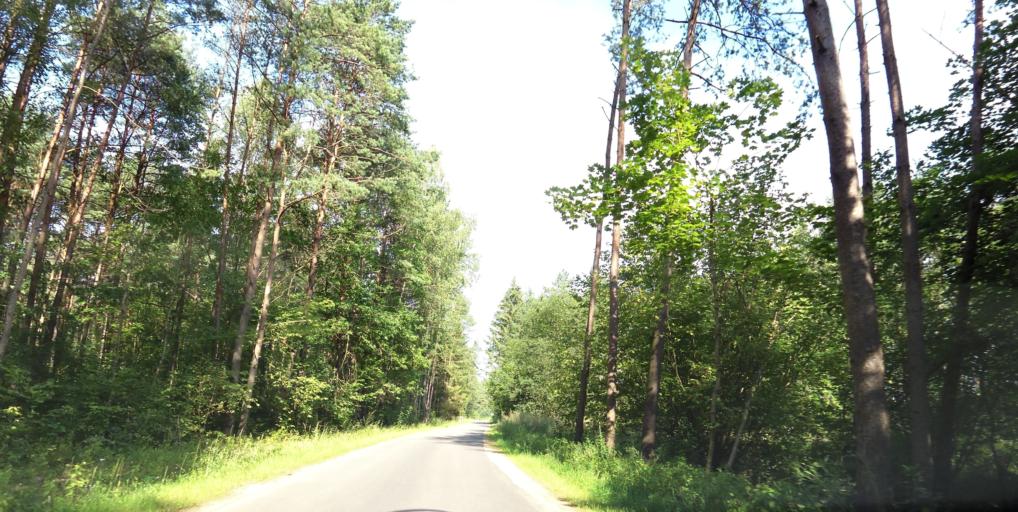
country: LT
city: Grigiskes
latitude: 54.7257
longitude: 25.0484
